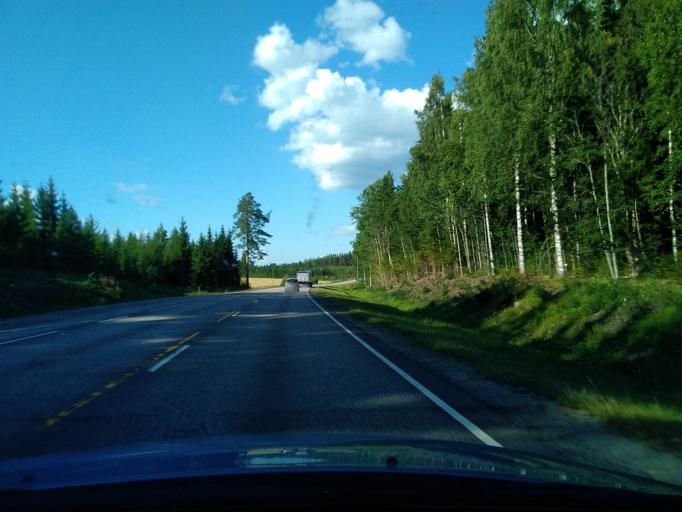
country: FI
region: Central Finland
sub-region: Keuruu
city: Keuruu
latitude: 62.1285
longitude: 24.7362
